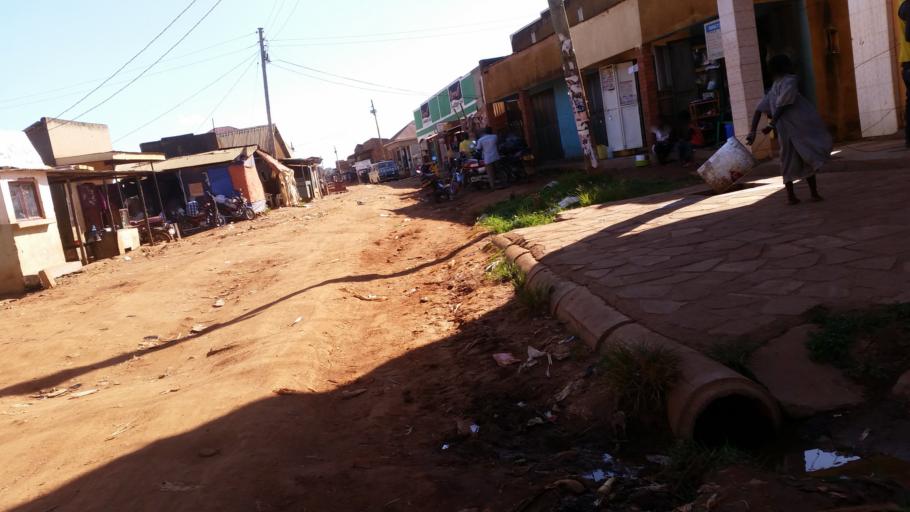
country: UG
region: Central Region
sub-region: Wakiso District
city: Kireka
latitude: 0.3298
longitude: 32.6516
